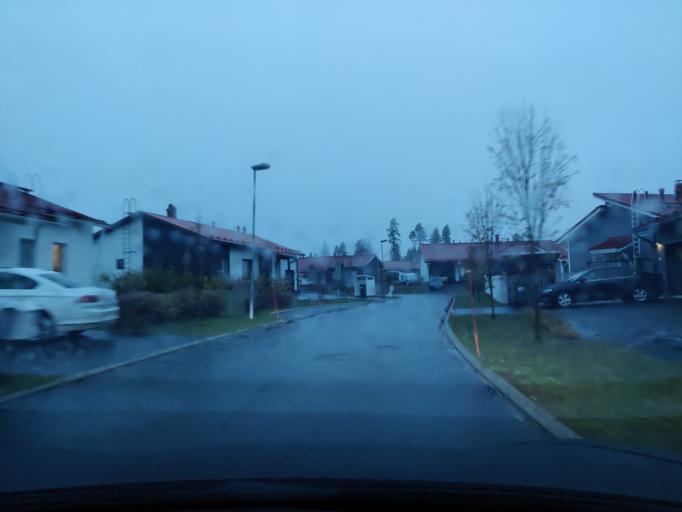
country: FI
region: Northern Savo
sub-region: Kuopio
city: Kuopio
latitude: 62.8267
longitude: 27.7224
